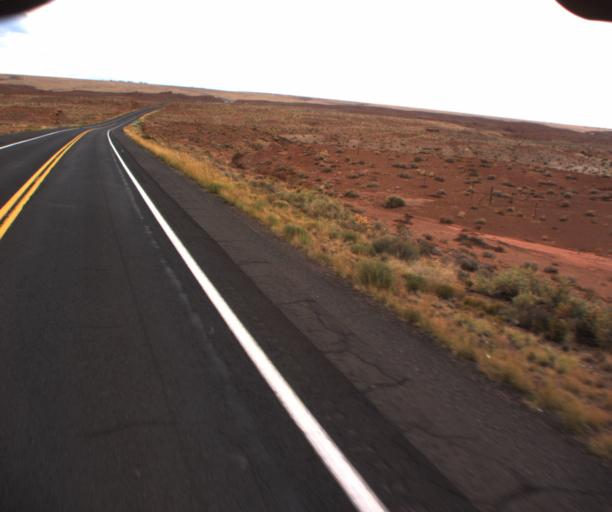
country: US
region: Arizona
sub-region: Coconino County
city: Tuba City
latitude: 35.7919
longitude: -111.4493
